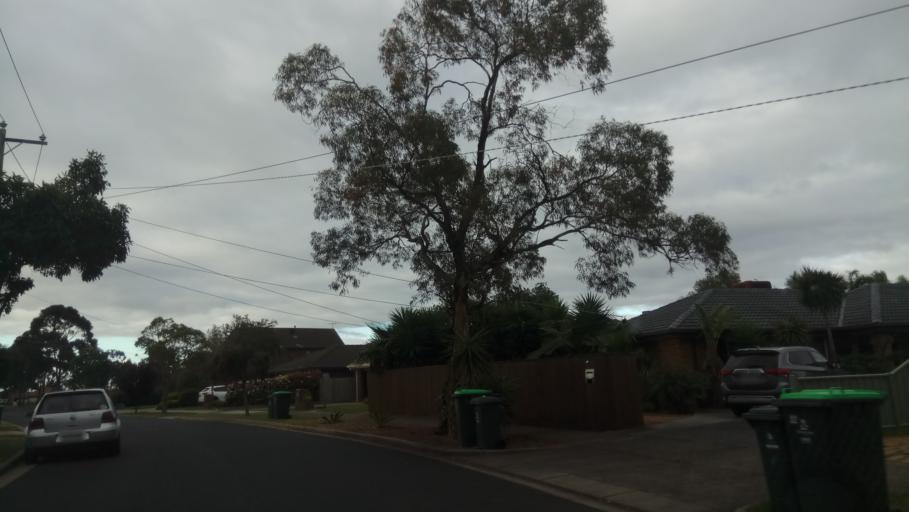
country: AU
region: Victoria
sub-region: Hobsons Bay
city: Altona Meadows
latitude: -37.8686
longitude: 144.7895
